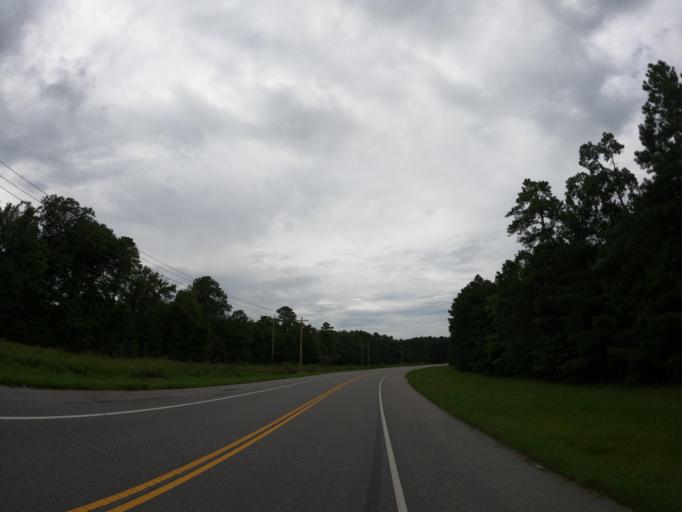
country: US
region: Maryland
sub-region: Saint Mary's County
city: Lexington Park
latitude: 38.1652
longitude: -76.5317
